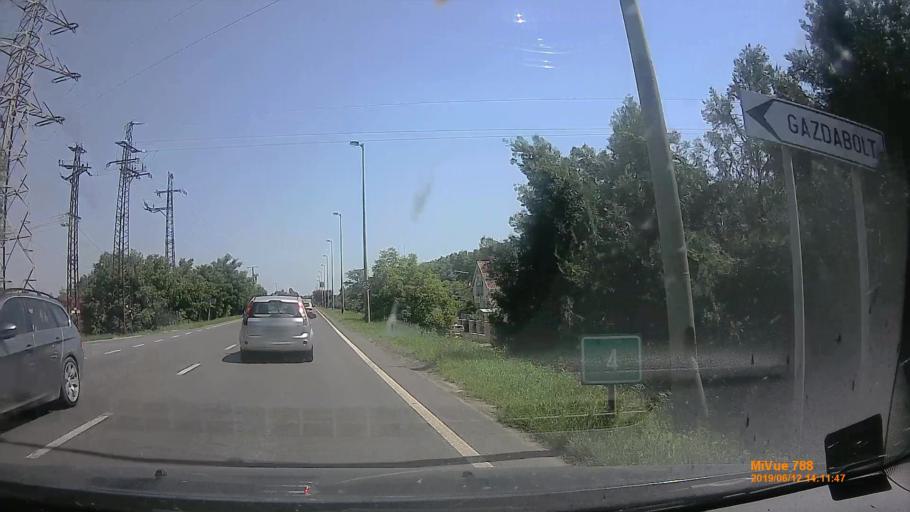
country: HU
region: Csongrad
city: Szeged
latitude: 46.2407
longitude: 20.1649
